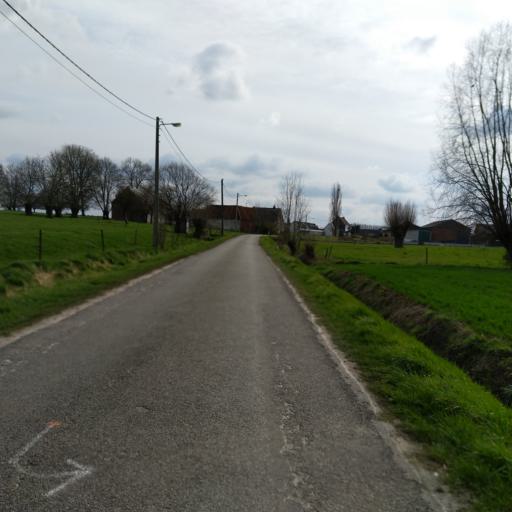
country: BE
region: Wallonia
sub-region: Province du Hainaut
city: Soignies
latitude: 50.5451
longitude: 4.0638
